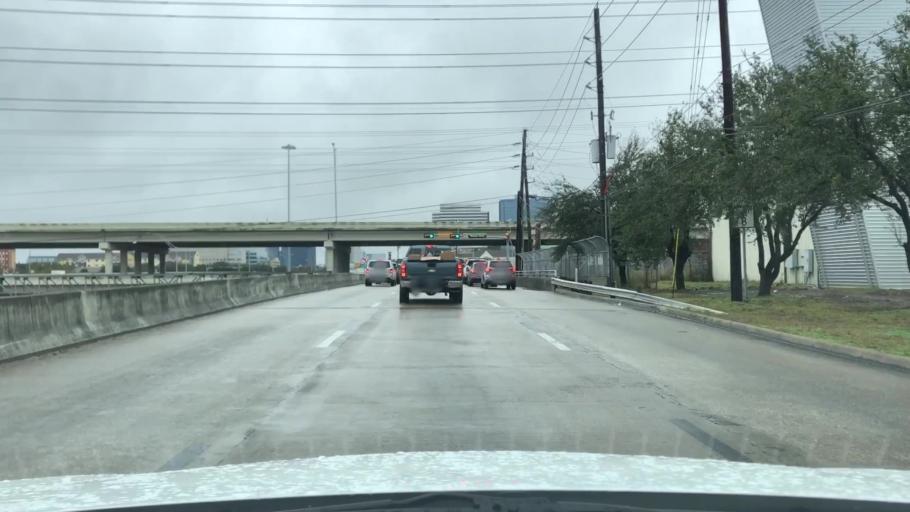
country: US
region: Texas
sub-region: Harris County
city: Bunker Hill Village
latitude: 29.7171
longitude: -95.5565
